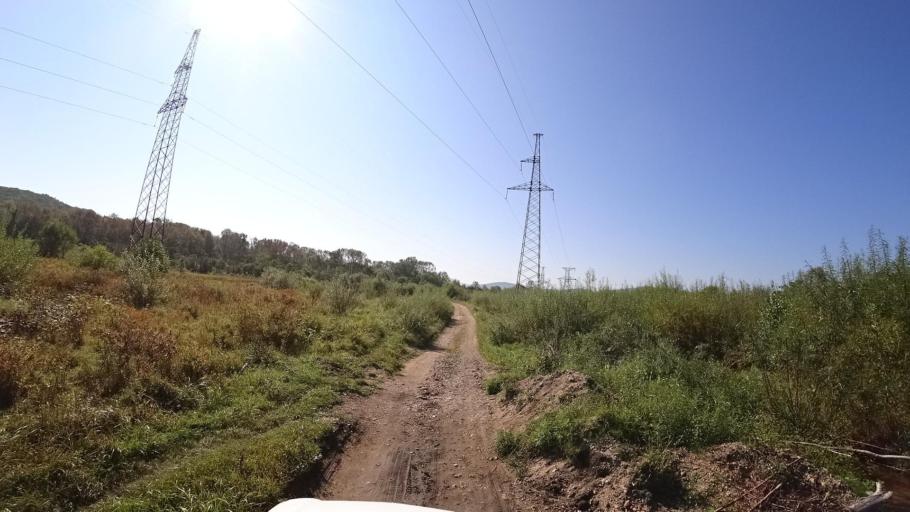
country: RU
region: Jewish Autonomous Oblast
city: Bira
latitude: 49.0013
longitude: 132.4766
